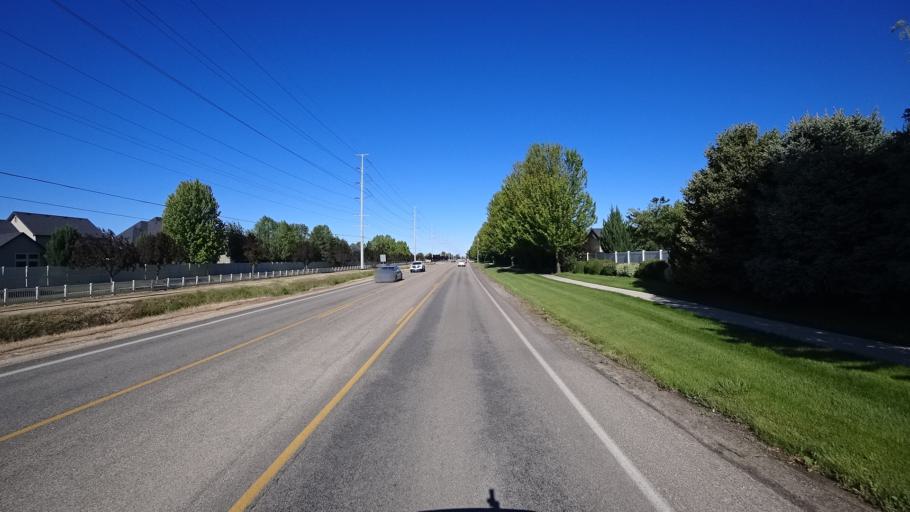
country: US
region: Idaho
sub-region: Ada County
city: Meridian
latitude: 43.6483
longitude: -116.4161
